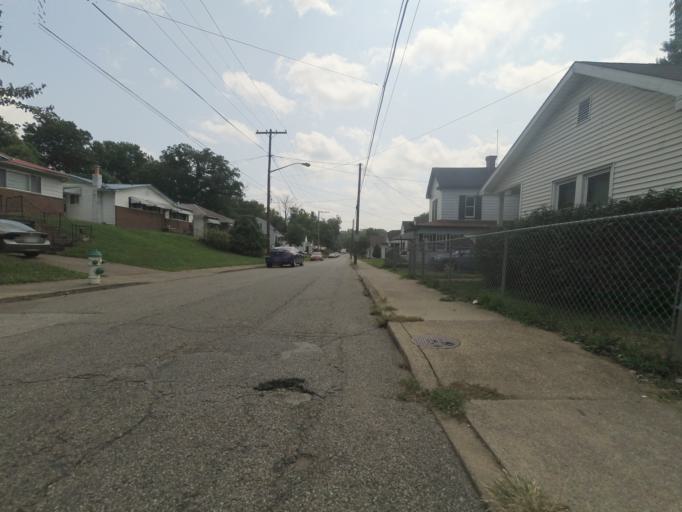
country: US
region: West Virginia
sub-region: Cabell County
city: Huntington
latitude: 38.4123
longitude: -82.4010
